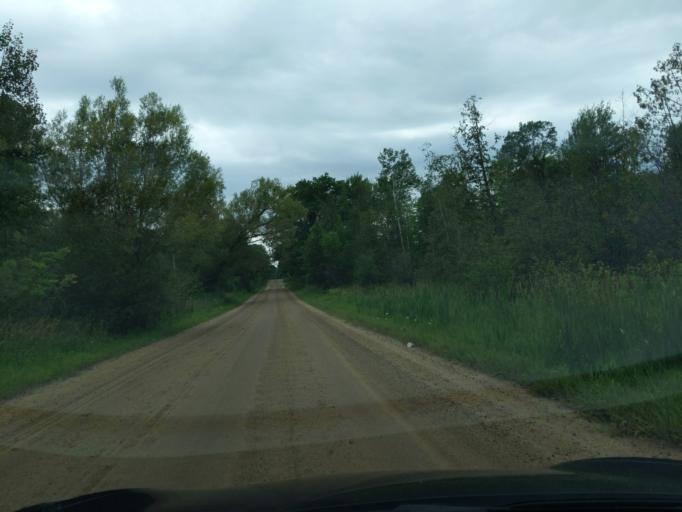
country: US
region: Michigan
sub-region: Clare County
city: Harrison
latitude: 44.0024
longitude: -84.9514
